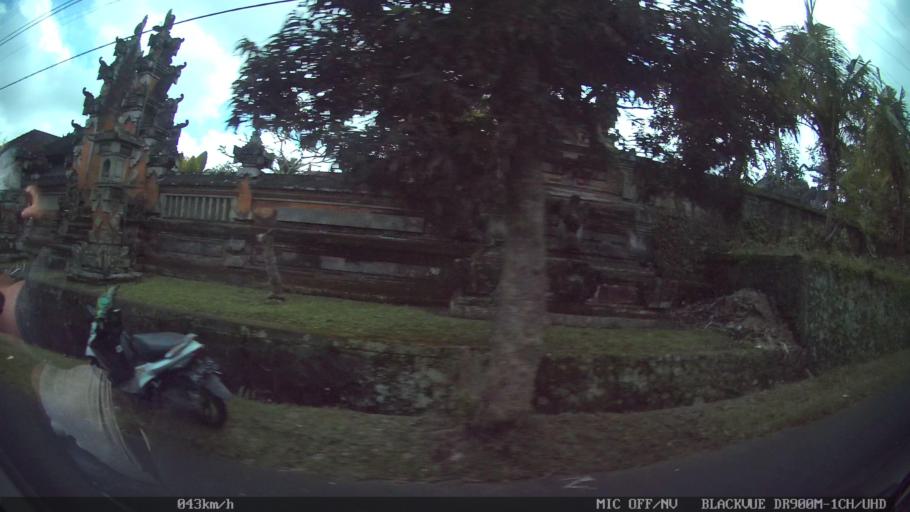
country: ID
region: Bali
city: Banjar Madangan Kaja
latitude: -8.4789
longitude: 115.3219
